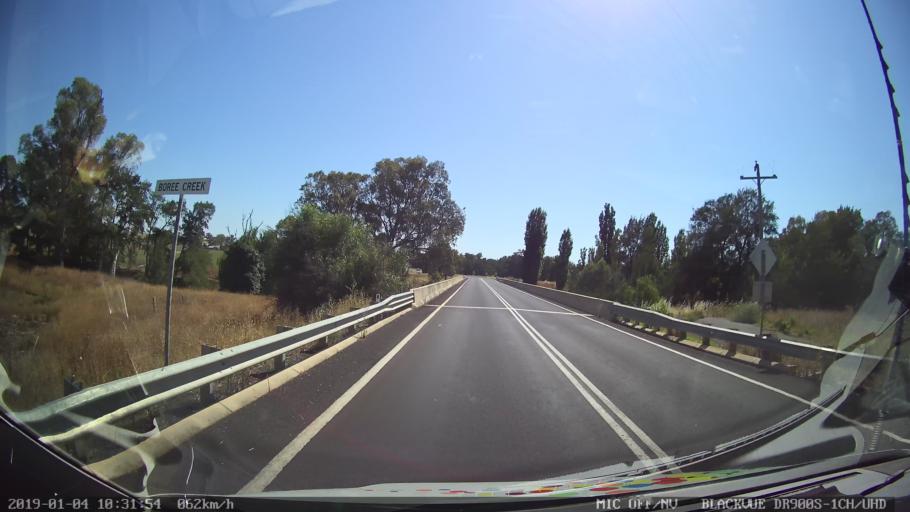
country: AU
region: New South Wales
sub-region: Cabonne
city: Canowindra
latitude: -33.3304
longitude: 148.6345
